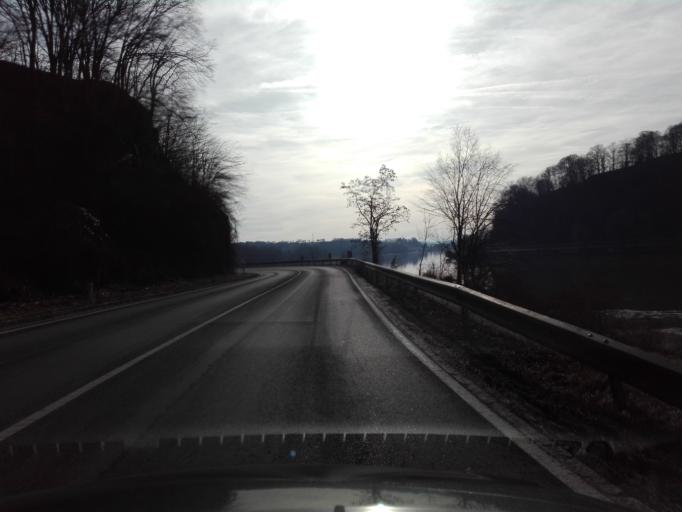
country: AT
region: Upper Austria
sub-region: Politischer Bezirk Perg
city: Bad Kreuzen
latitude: 48.1994
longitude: 14.8483
